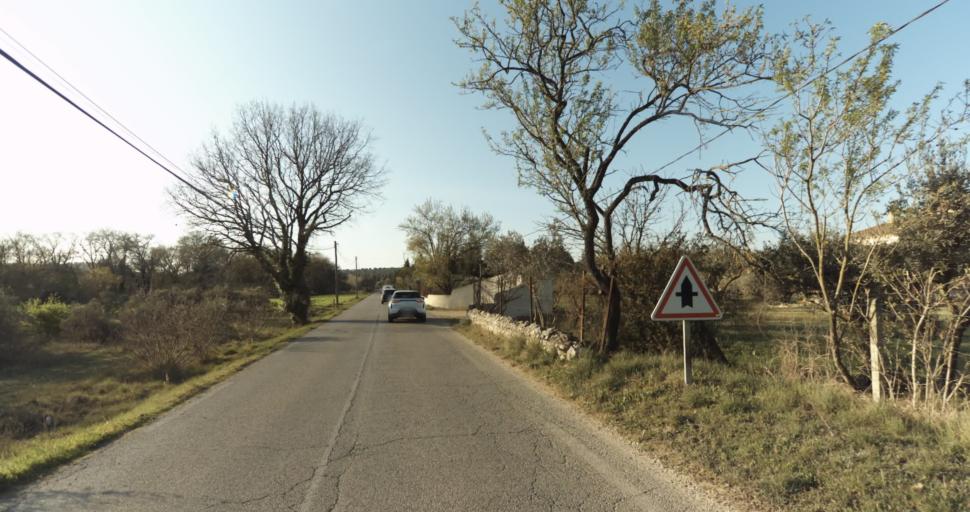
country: FR
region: Provence-Alpes-Cote d'Azur
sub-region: Departement des Bouches-du-Rhone
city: Ventabren
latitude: 43.5333
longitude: 5.2807
